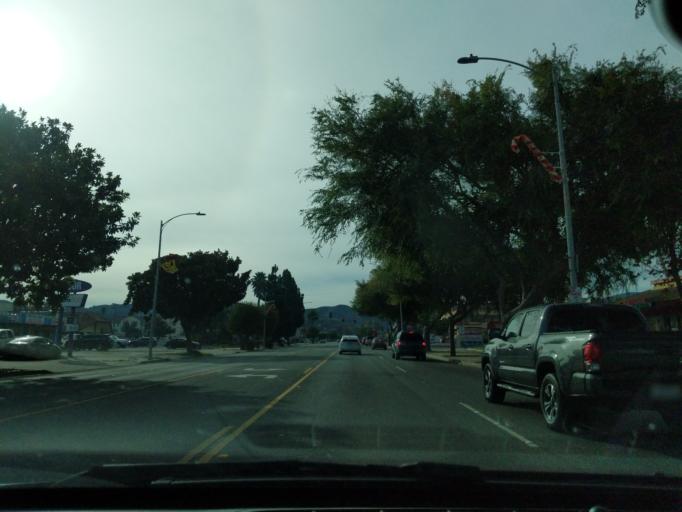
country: US
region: California
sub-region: Santa Barbara County
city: Lompoc
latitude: 34.6484
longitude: -120.4578
